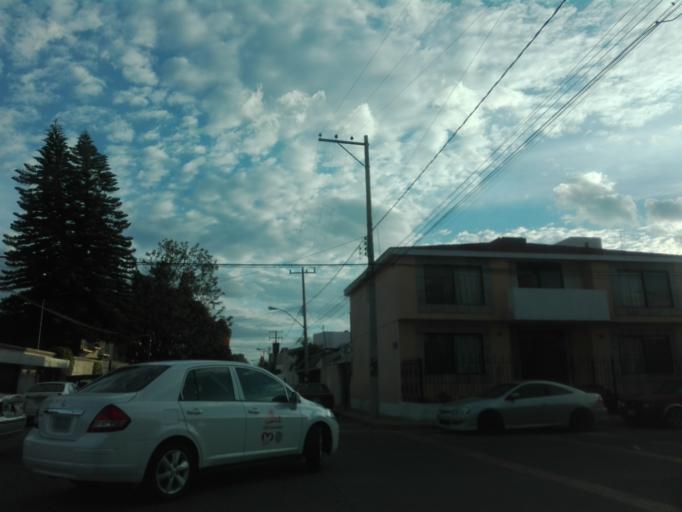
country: MX
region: Guanajuato
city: Leon
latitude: 21.1159
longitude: -101.6625
